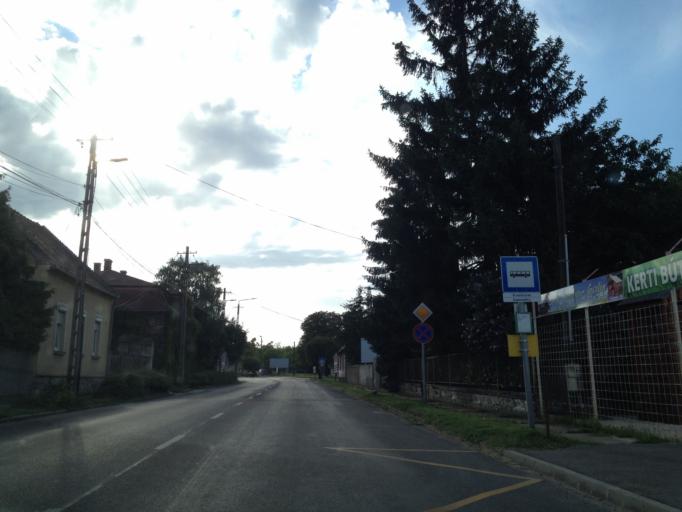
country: HU
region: Komarom-Esztergom
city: Komarom
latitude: 47.7477
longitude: 18.1054
